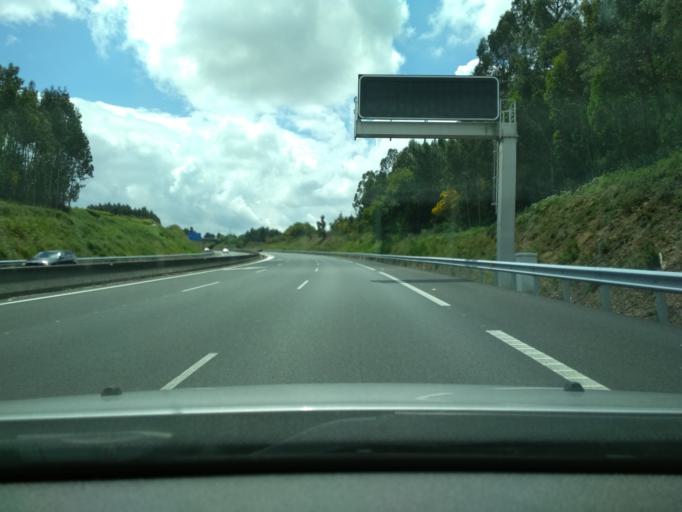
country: ES
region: Galicia
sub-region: Provincia de Pontevedra
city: Barro
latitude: 42.5274
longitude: -8.6705
